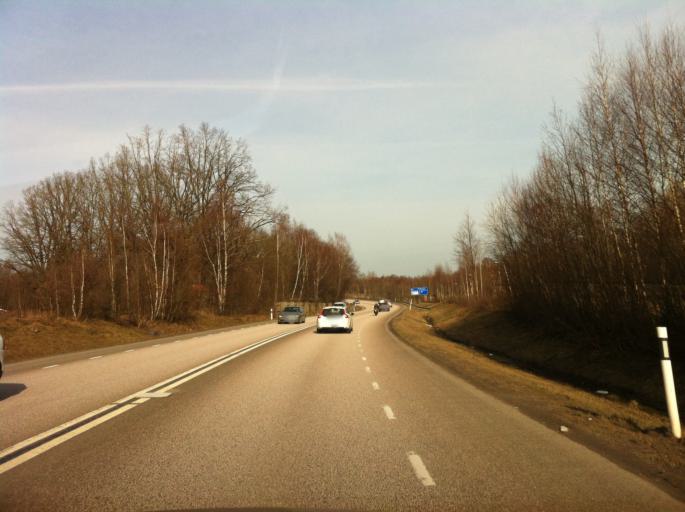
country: SE
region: Vaestra Goetaland
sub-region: Skovde Kommun
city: Skoevde
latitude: 58.4157
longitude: 13.8826
